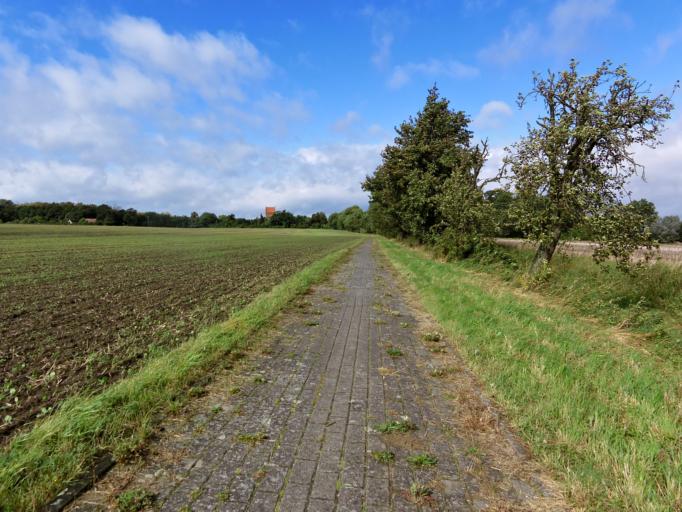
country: DE
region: Saxony-Anhalt
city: Hohenberg-Krusemark
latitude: 52.7499
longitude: 12.0133
